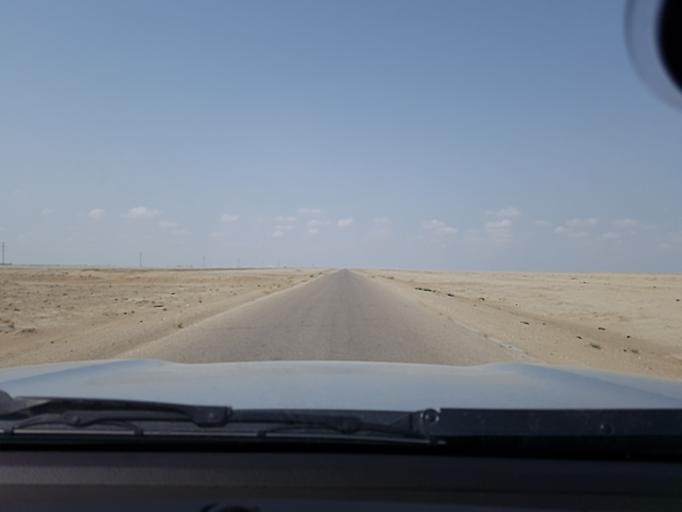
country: TM
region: Balkan
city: Gumdag
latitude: 38.6529
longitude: 54.3875
